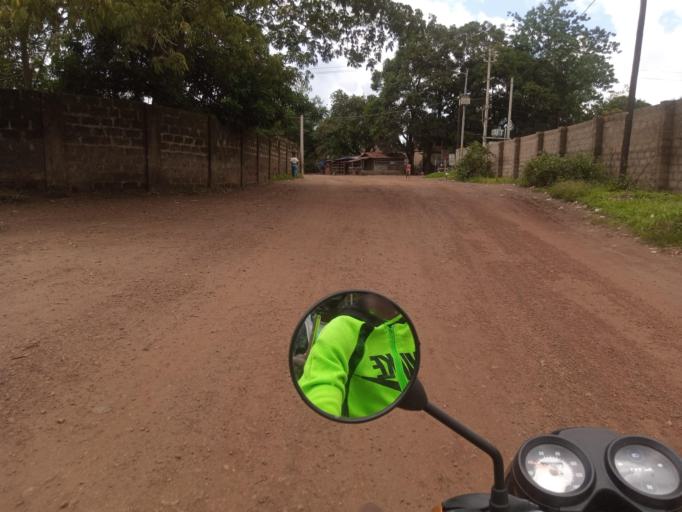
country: SL
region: Northern Province
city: Port Loko
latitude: 8.7648
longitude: -12.7812
